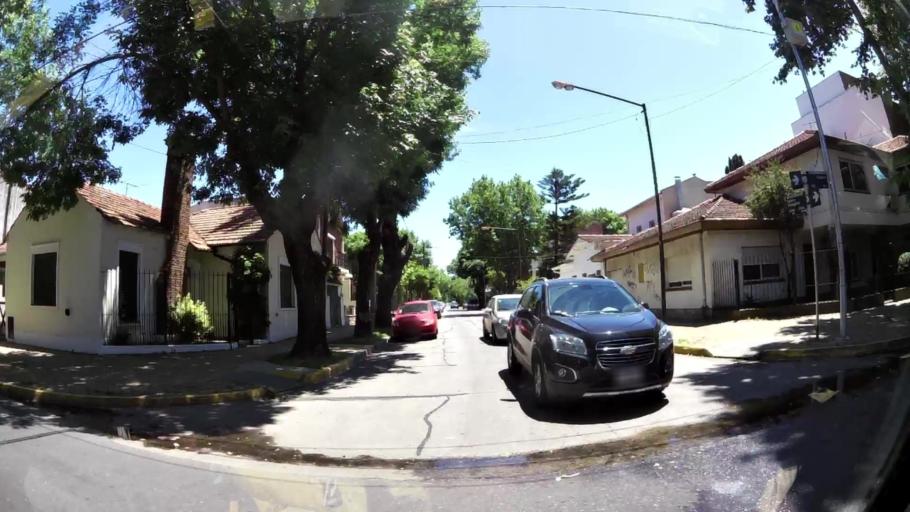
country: AR
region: Buenos Aires
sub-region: Partido de Vicente Lopez
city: Olivos
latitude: -34.4943
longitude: -58.5021
